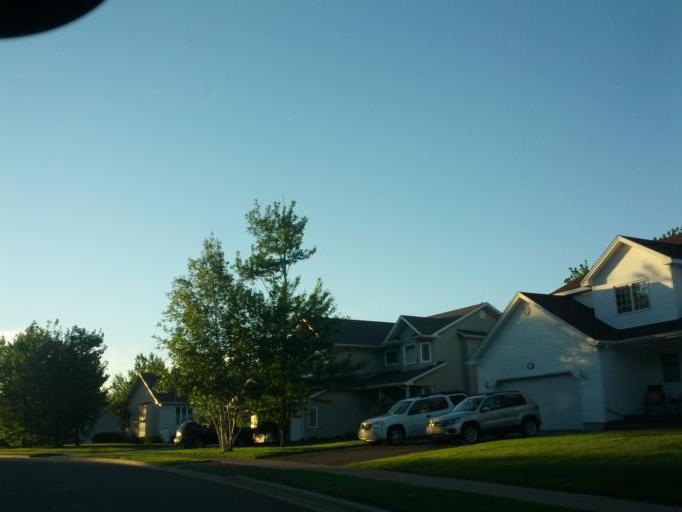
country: CA
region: New Brunswick
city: Moncton
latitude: 46.1158
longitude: -64.8681
